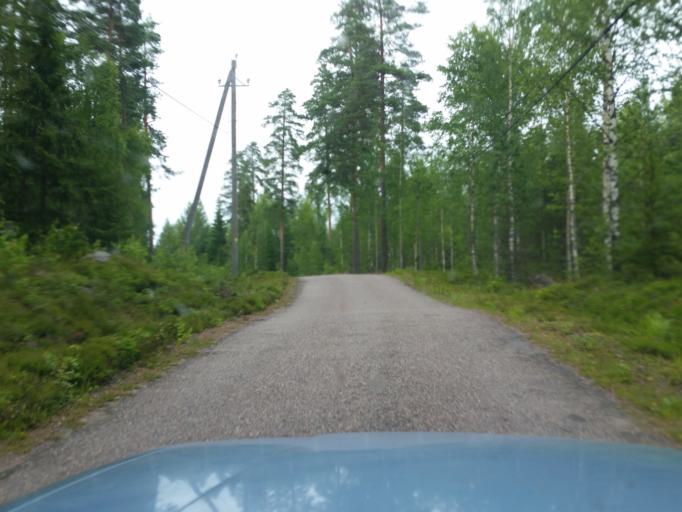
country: FI
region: Uusimaa
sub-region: Helsinki
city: Kaerkoelae
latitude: 60.5580
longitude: 24.0032
